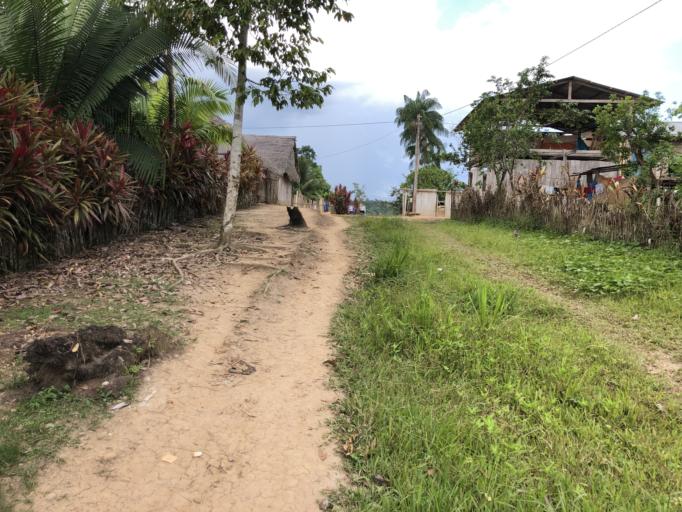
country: PE
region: Loreto
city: Puerto Galilea
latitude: -4.0569
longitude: -77.7562
